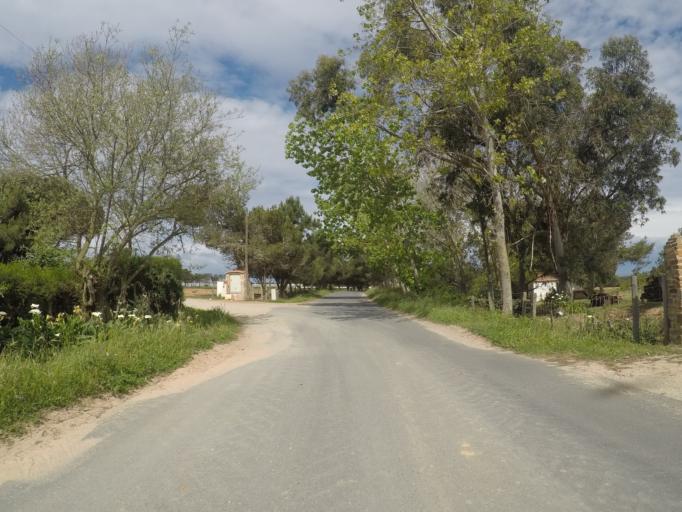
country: PT
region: Beja
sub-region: Odemira
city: Sao Teotonio
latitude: 37.4952
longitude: -8.7872
